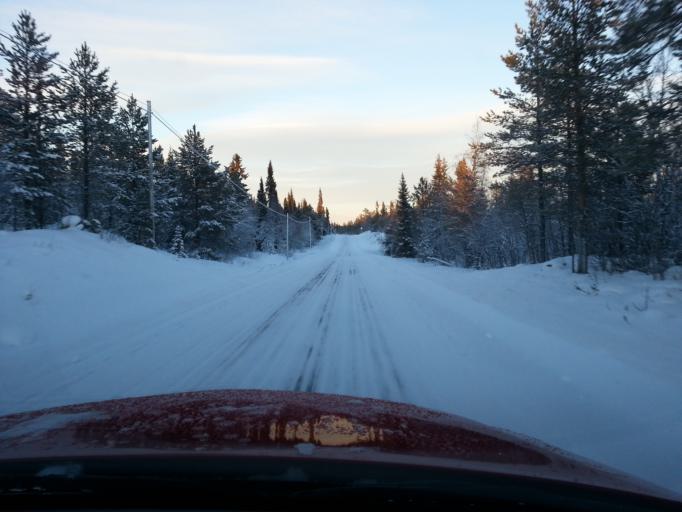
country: SE
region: Jaemtland
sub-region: Harjedalens Kommun
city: Sveg
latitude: 62.2875
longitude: 13.3996
